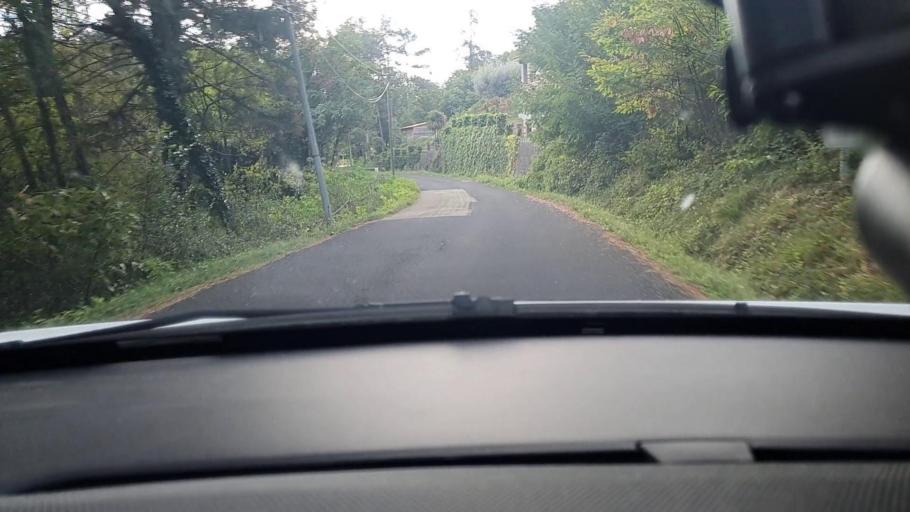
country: FR
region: Languedoc-Roussillon
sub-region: Departement du Gard
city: Besseges
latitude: 44.3160
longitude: 4.0840
